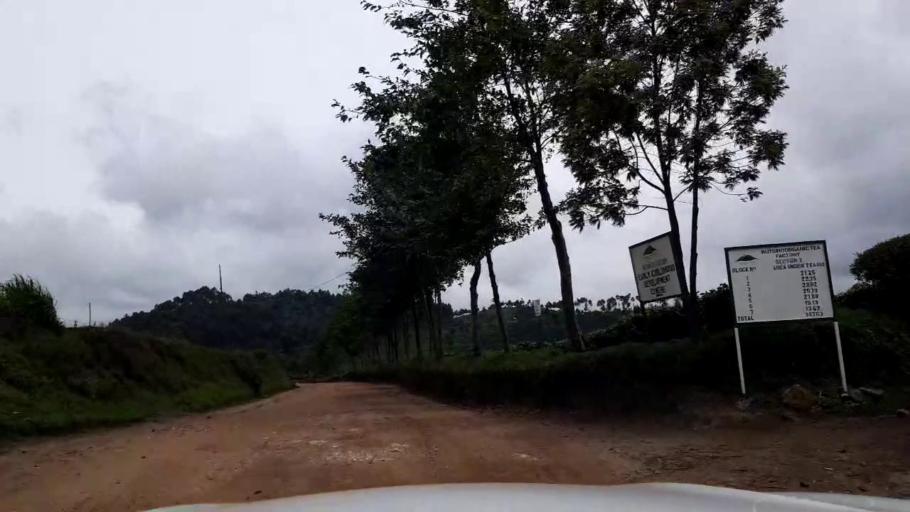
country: RW
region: Western Province
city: Kibuye
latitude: -1.9540
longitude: 29.4058
